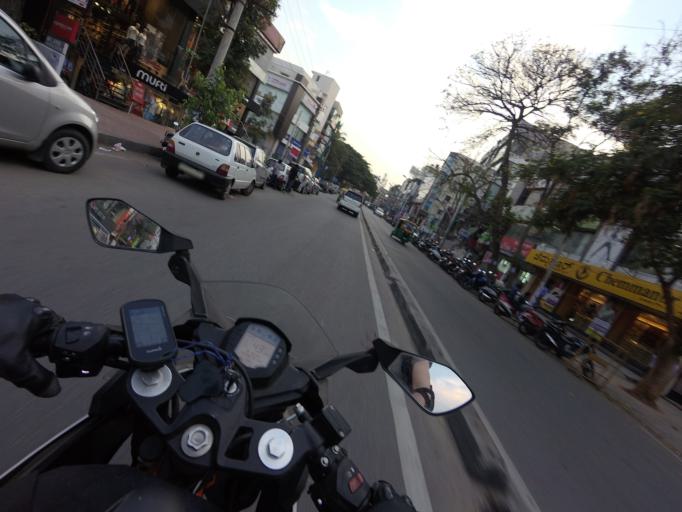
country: IN
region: Karnataka
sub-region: Bangalore Urban
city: Bangalore
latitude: 13.0242
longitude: 77.6371
